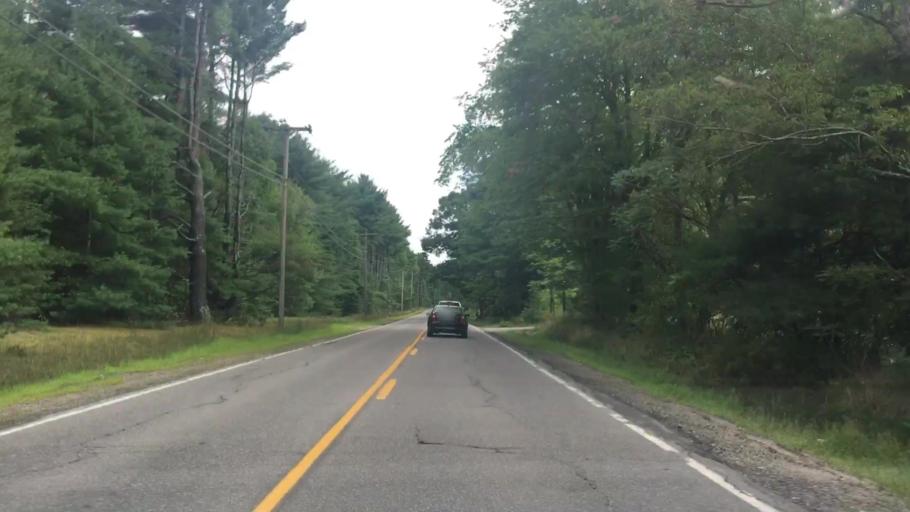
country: US
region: Maine
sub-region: York County
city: Lake Arrowhead
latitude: 43.6124
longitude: -70.7181
